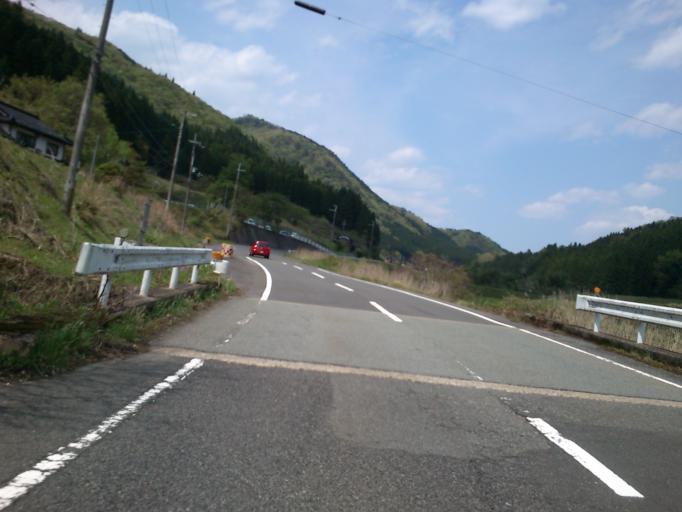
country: JP
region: Kyoto
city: Fukuchiyama
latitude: 35.3821
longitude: 134.9398
